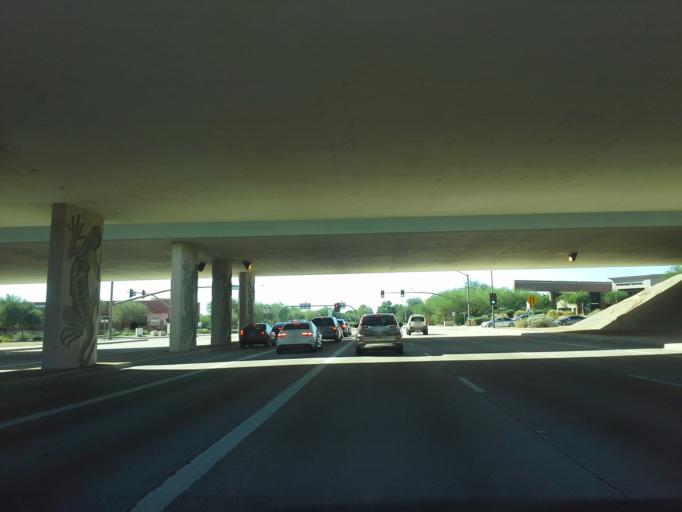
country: US
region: Arizona
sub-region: Maricopa County
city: Paradise Valley
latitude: 33.6402
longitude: -111.8901
